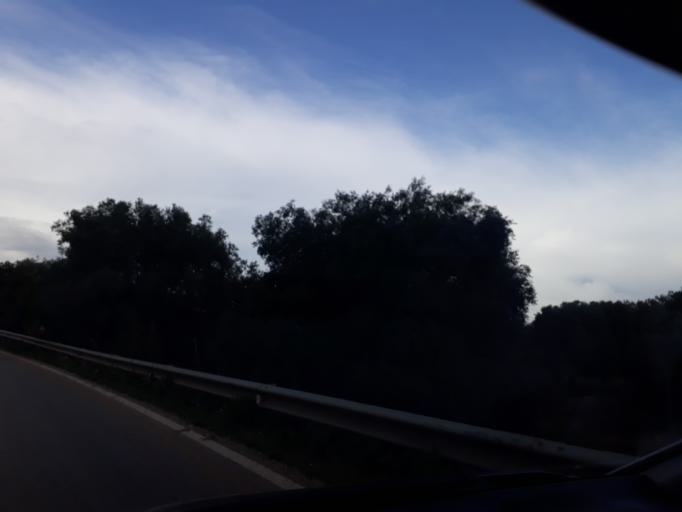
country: IT
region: Apulia
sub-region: Provincia di Brindisi
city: Fasano
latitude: 40.8208
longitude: 17.3764
